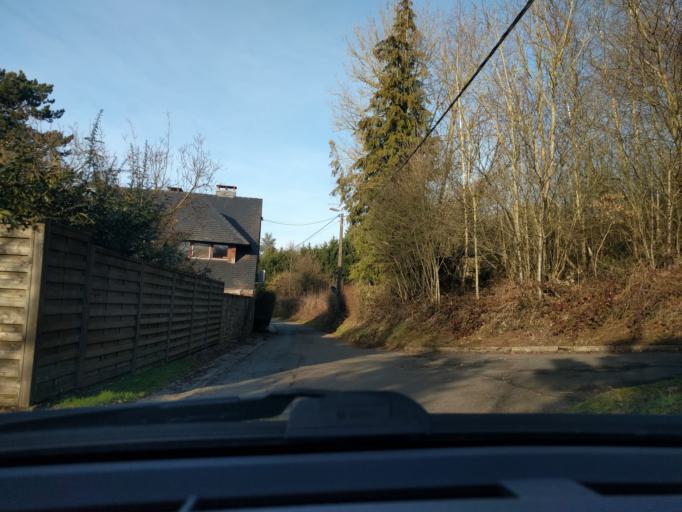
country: BE
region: Wallonia
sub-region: Province de Namur
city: Couvin
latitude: 50.0395
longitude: 4.5059
